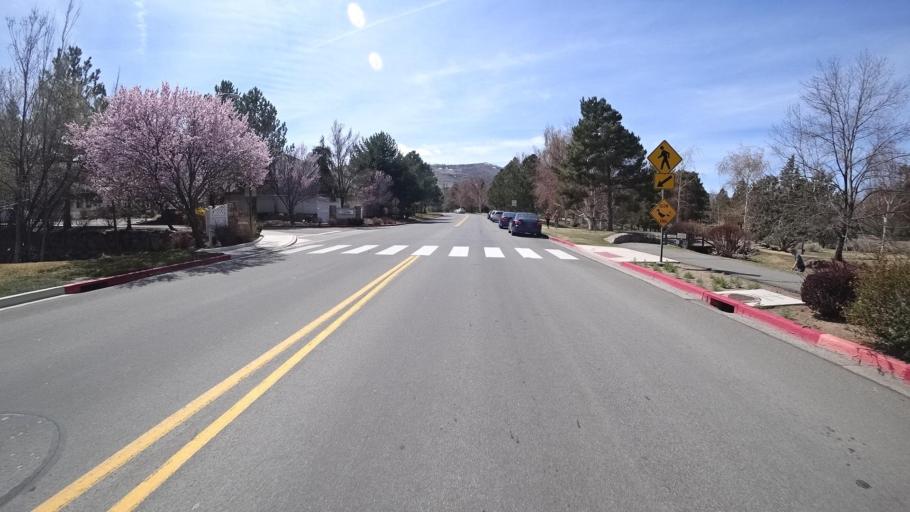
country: US
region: Nevada
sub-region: Washoe County
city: Reno
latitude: 39.5010
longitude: -119.8614
